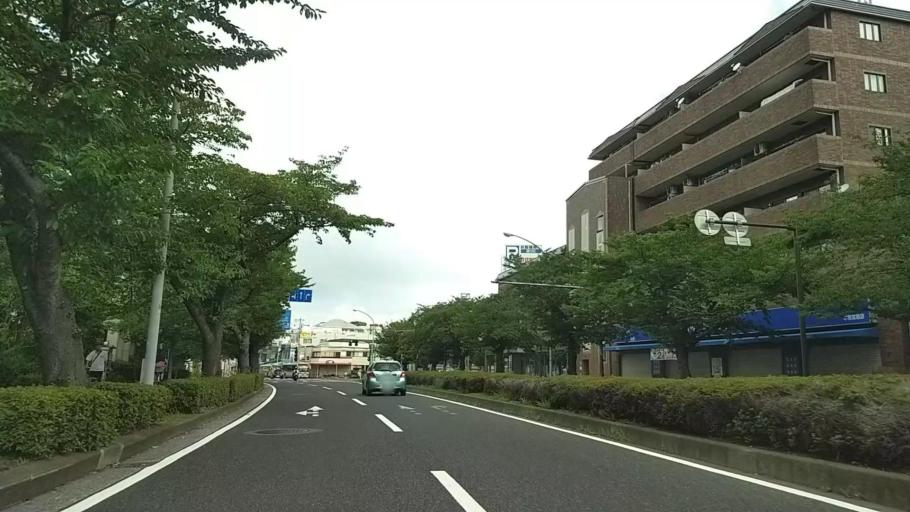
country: JP
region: Kanagawa
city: Yokohama
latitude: 35.4285
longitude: 139.6647
